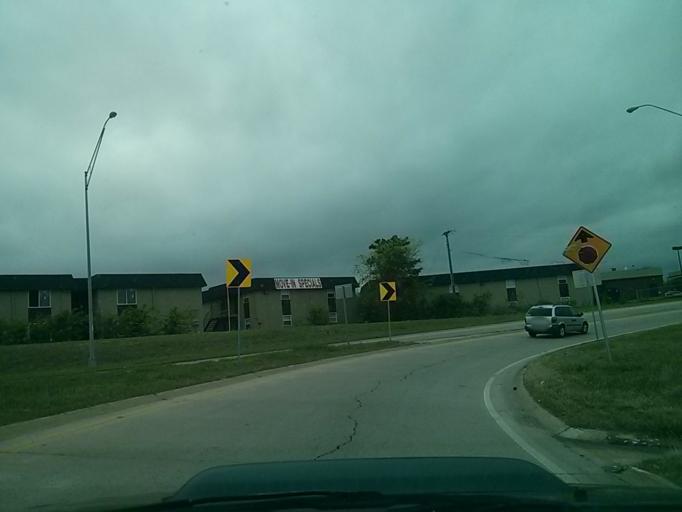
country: US
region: Oklahoma
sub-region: Tulsa County
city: Owasso
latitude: 36.1657
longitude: -95.8499
